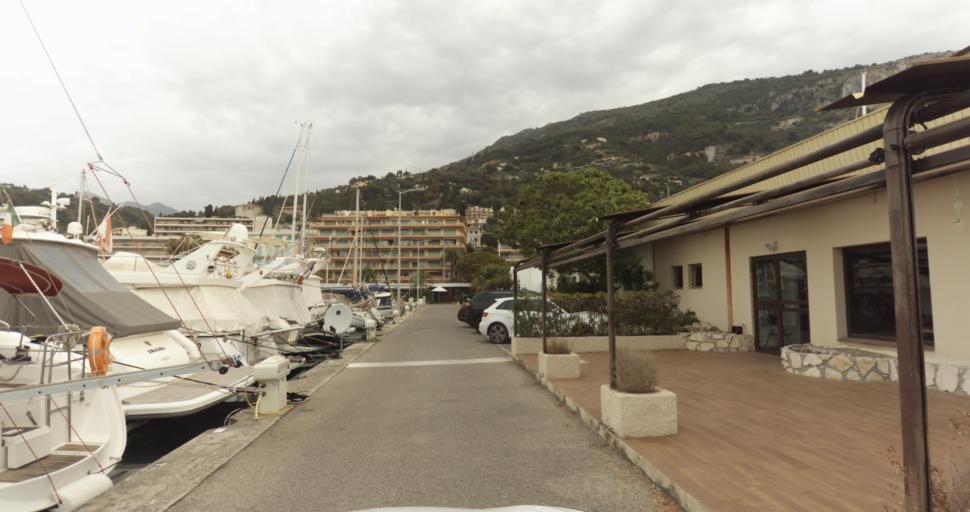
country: FR
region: Provence-Alpes-Cote d'Azur
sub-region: Departement des Alpes-Maritimes
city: Menton
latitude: 43.7837
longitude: 7.5202
